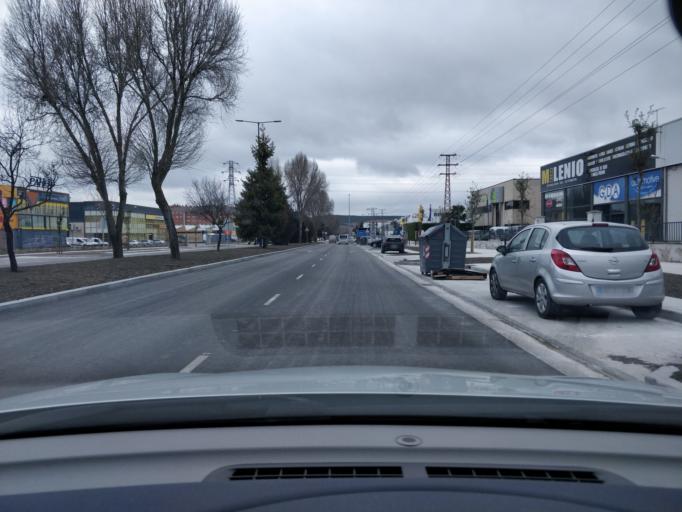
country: ES
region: Castille and Leon
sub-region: Provincia de Burgos
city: Burgos
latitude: 42.3591
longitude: -3.6515
